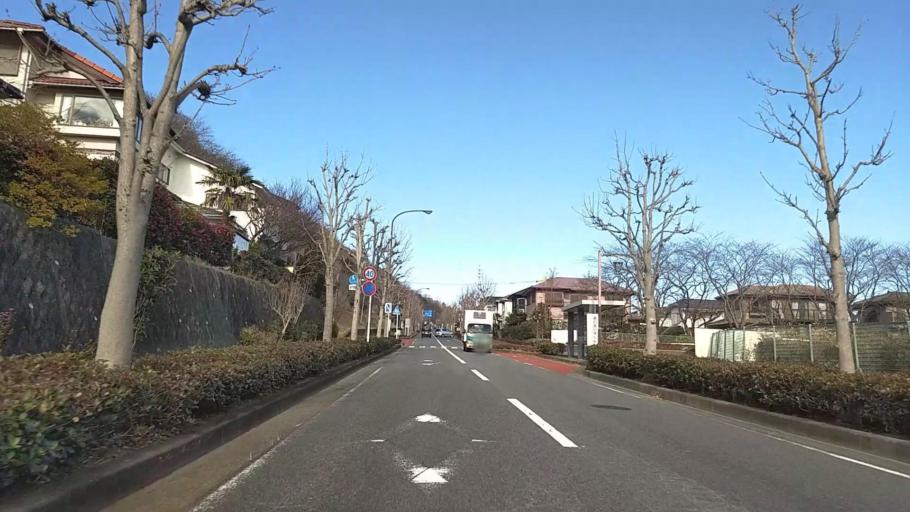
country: JP
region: Kanagawa
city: Isehara
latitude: 35.4446
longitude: 139.3057
